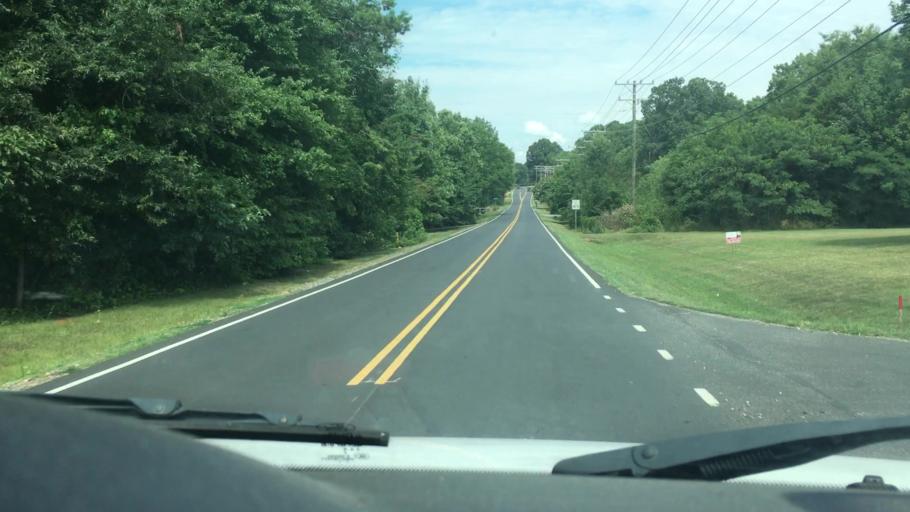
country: US
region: North Carolina
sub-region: Gaston County
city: Davidson
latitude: 35.5391
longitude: -80.8356
